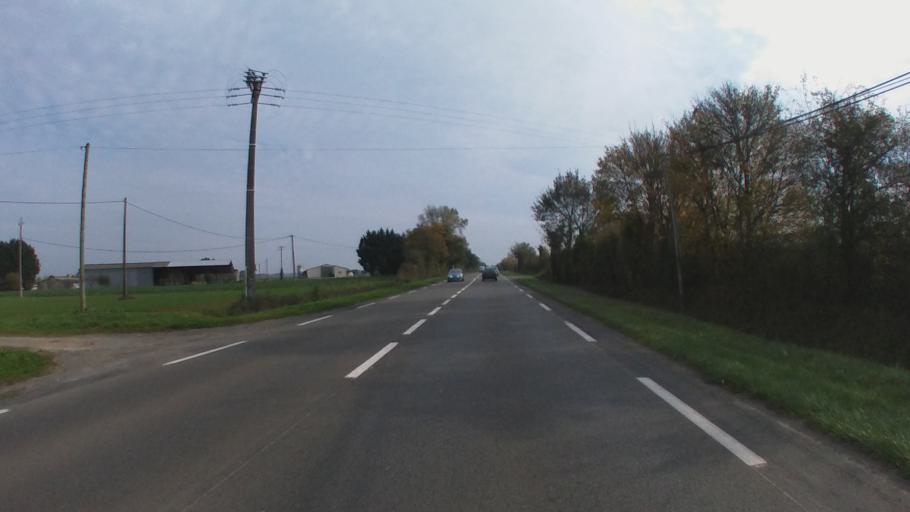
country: FR
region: Pays de la Loire
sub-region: Departement de la Sarthe
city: Vion
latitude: 47.7876
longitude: -0.2415
